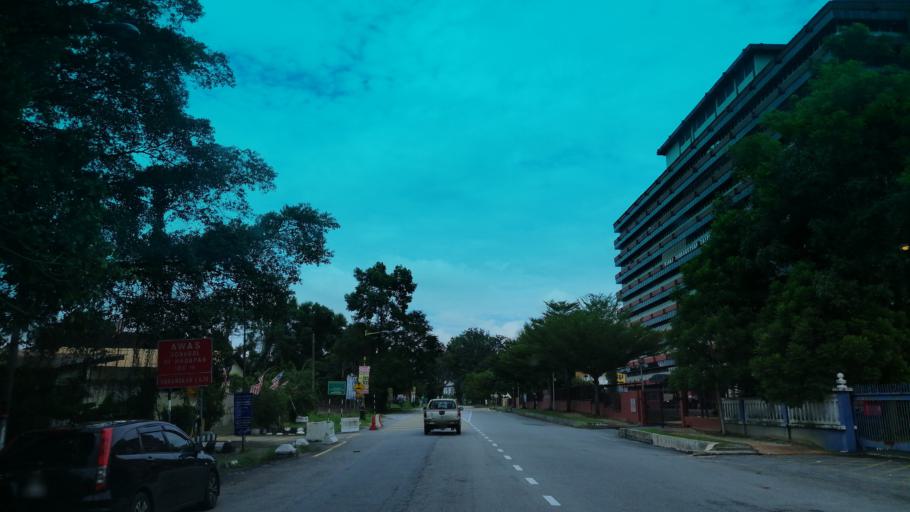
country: MY
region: Perak
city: Taiping
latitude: 4.8561
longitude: 100.7400
